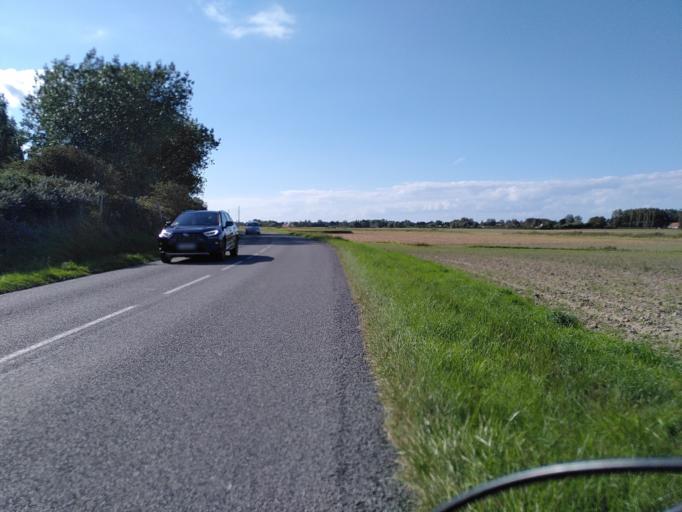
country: FR
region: Nord-Pas-de-Calais
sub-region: Departement du Pas-de-Calais
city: Oye-Plage
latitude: 50.9879
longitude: 2.0116
